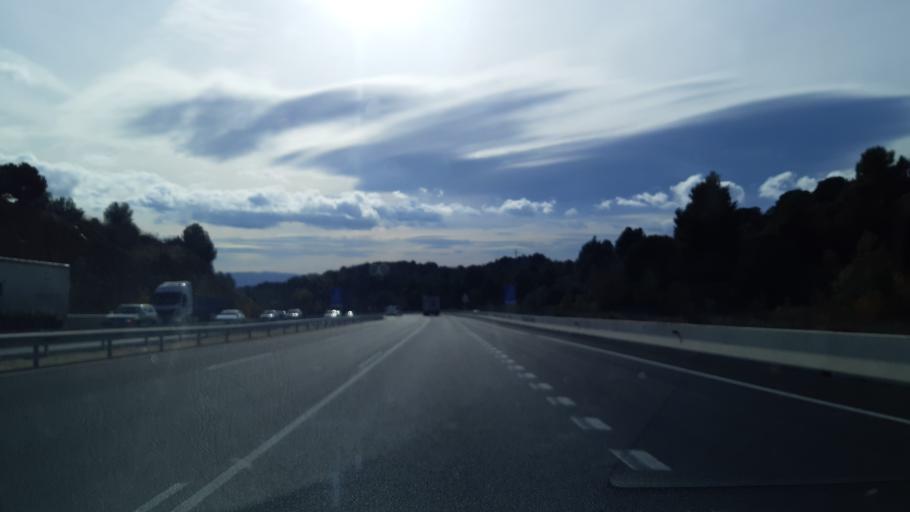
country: ES
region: Catalonia
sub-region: Provincia de Barcelona
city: Collbato
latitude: 41.5882
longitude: 1.7727
